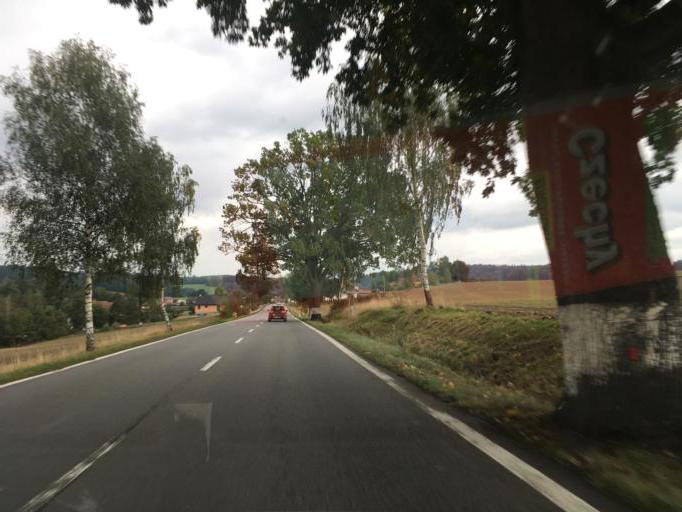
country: CZ
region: Vysocina
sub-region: Okres Pelhrimov
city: Pelhrimov
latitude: 49.3825
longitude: 15.2531
